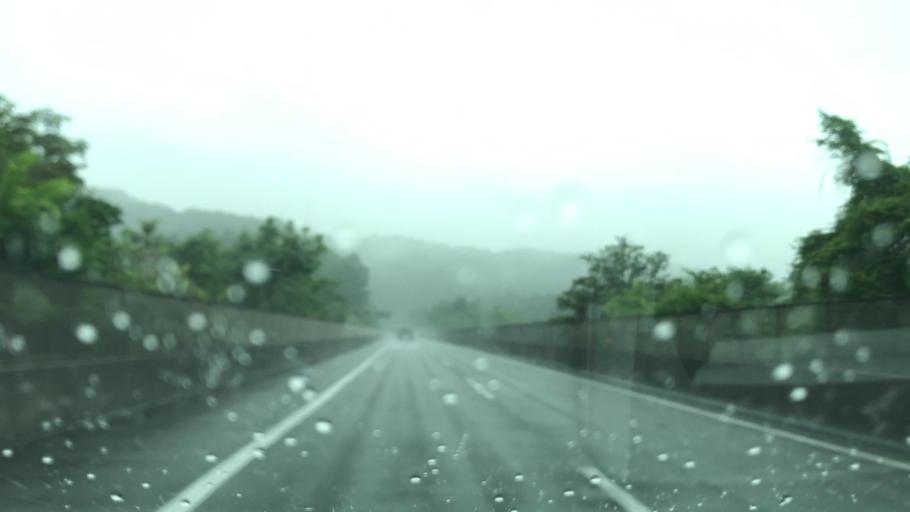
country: JP
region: Hokkaido
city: Shiraoi
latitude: 42.5736
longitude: 141.3573
